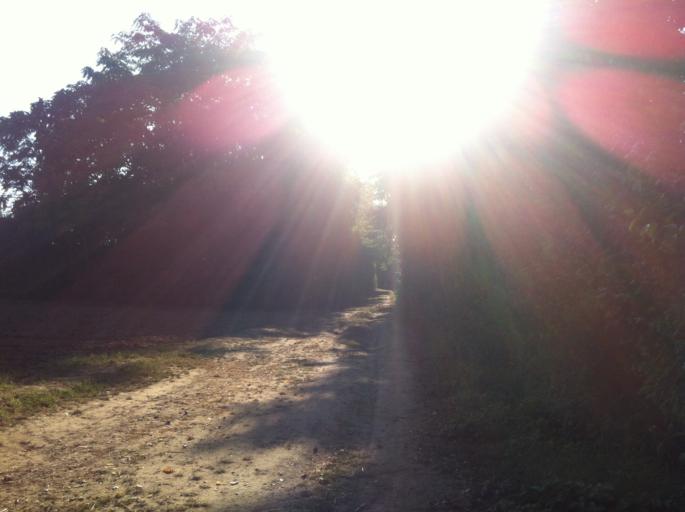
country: DE
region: Rheinland-Pfalz
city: Klein-Winternheim
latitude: 49.9712
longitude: 8.2042
